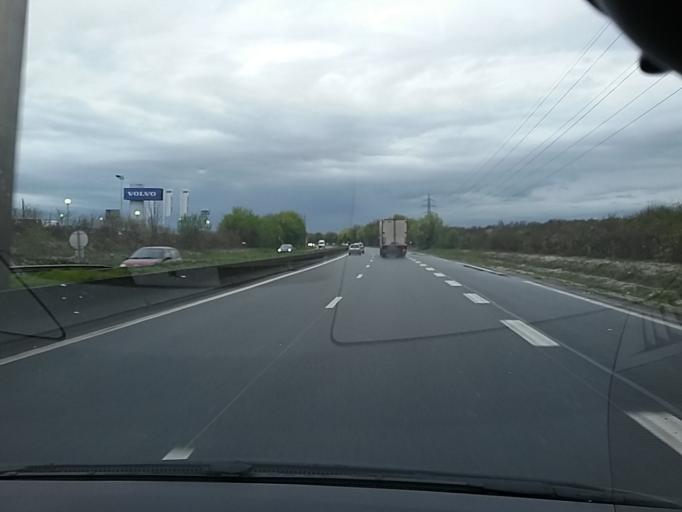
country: FR
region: Picardie
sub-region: Departement de la Somme
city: Rivery
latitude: 49.9165
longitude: 2.3404
